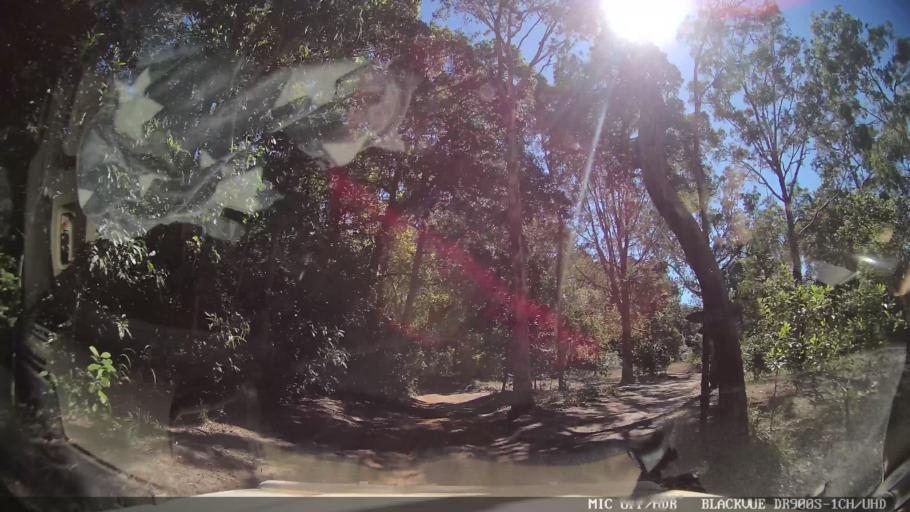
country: AU
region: Queensland
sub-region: Torres
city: Thursday Island
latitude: -10.8280
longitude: 142.3997
